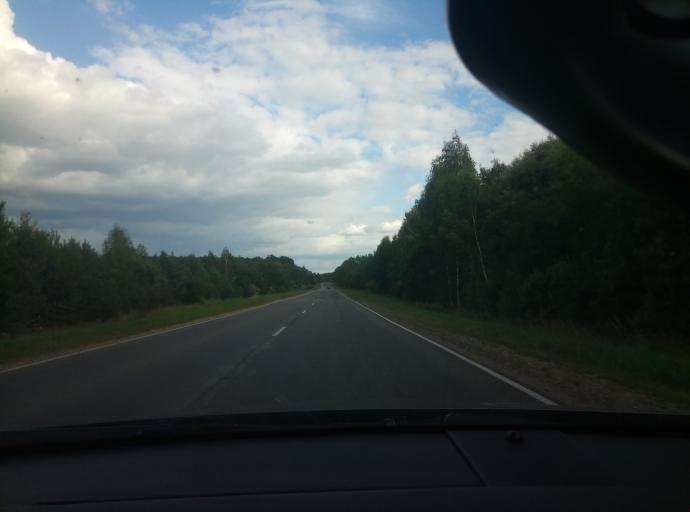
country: RU
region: Kaluga
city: Nikola-Lenivets
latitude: 54.5418
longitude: 35.5430
